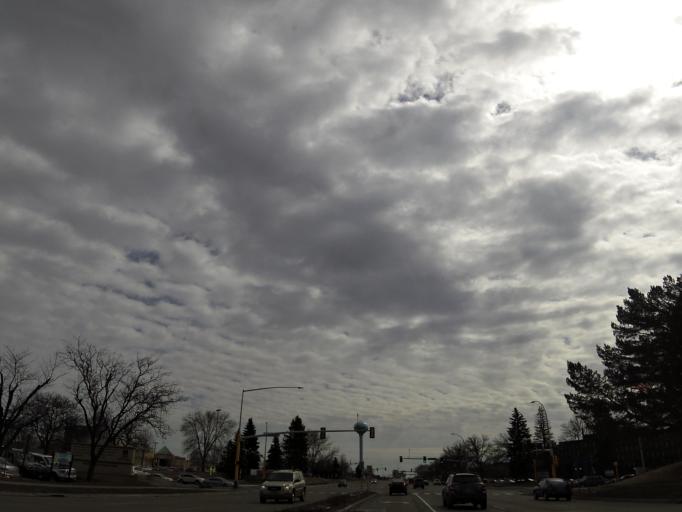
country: US
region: Minnesota
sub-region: Hennepin County
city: Edina
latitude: 44.8843
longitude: -93.3290
